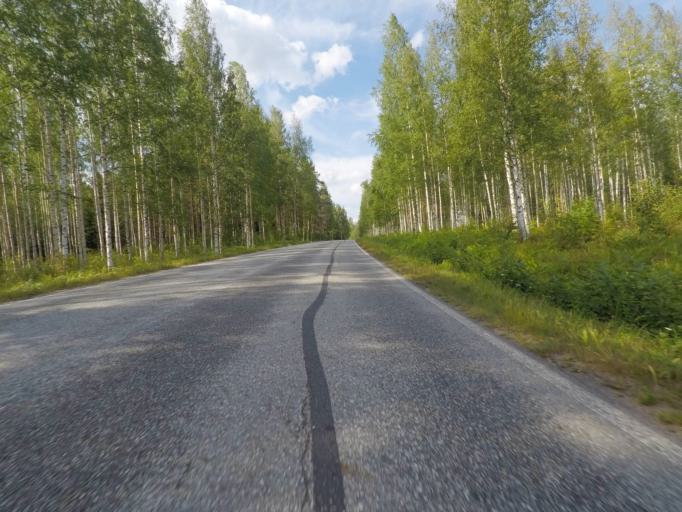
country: FI
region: Southern Savonia
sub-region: Mikkeli
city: Puumala
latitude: 61.7048
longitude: 28.2112
